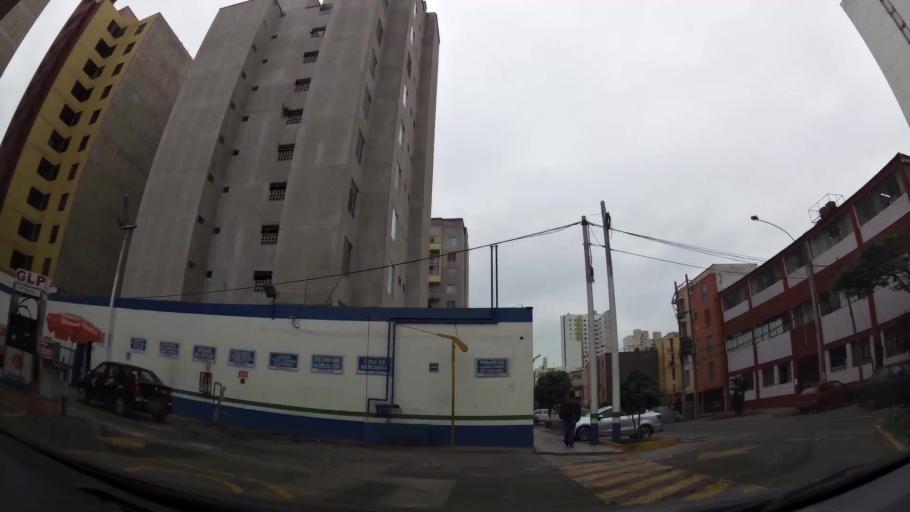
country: PE
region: Lima
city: Lima
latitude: -12.0664
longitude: -77.0462
